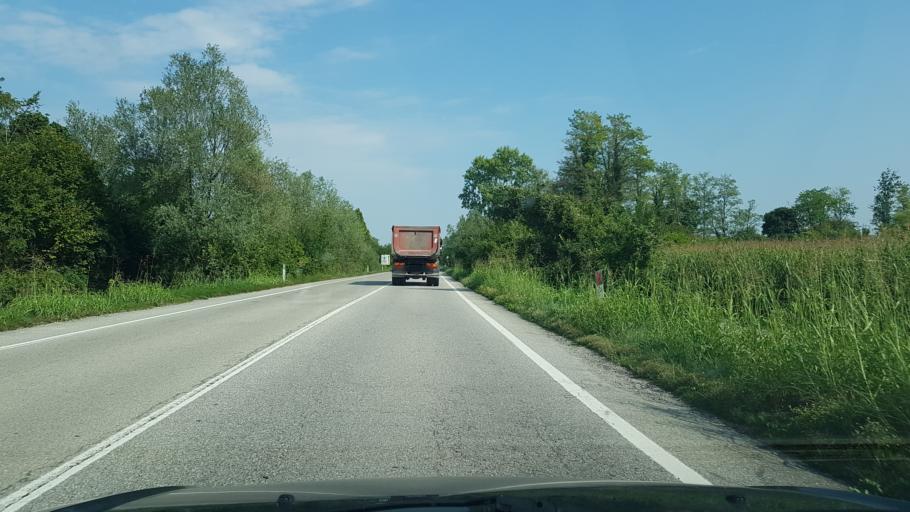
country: IT
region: Friuli Venezia Giulia
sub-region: Provincia di Pordenone
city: Spilimbergo
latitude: 46.0986
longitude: 12.8634
